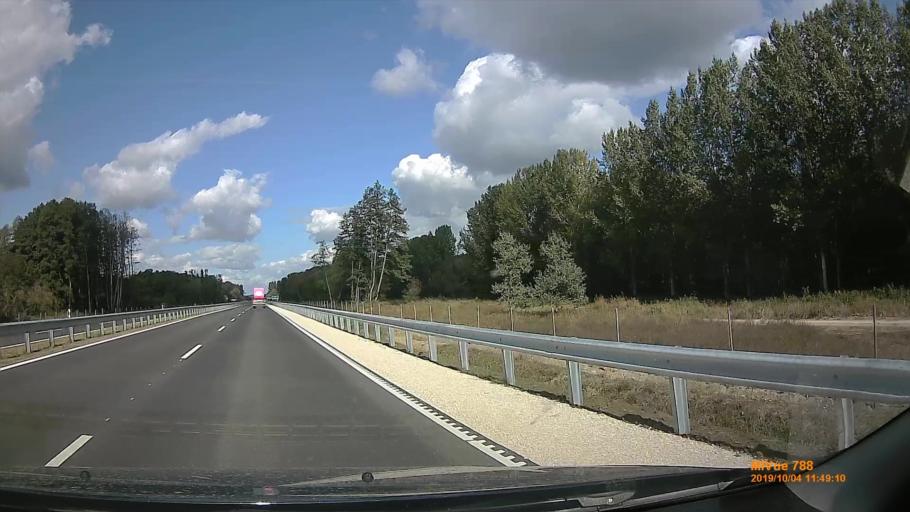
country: HU
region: Somogy
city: Karad
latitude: 46.6702
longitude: 17.7810
